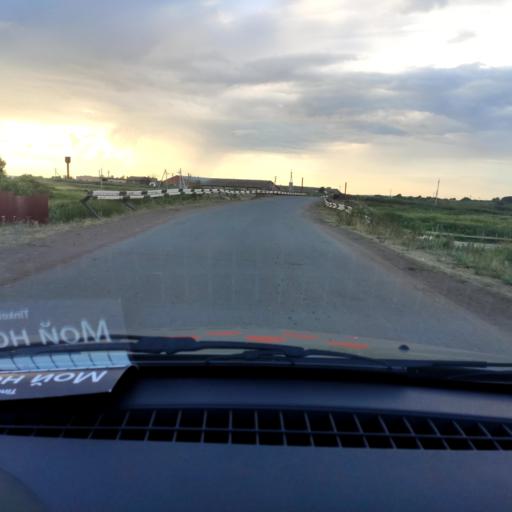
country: RU
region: Bashkortostan
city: Mikhaylovka
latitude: 54.9699
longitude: 55.7885
